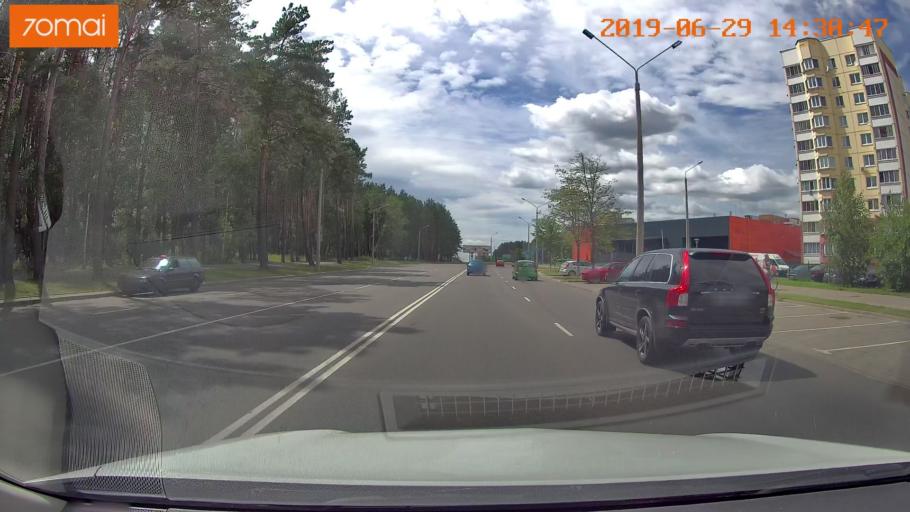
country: BY
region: Minsk
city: Salihorsk
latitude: 52.7814
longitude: 27.5140
